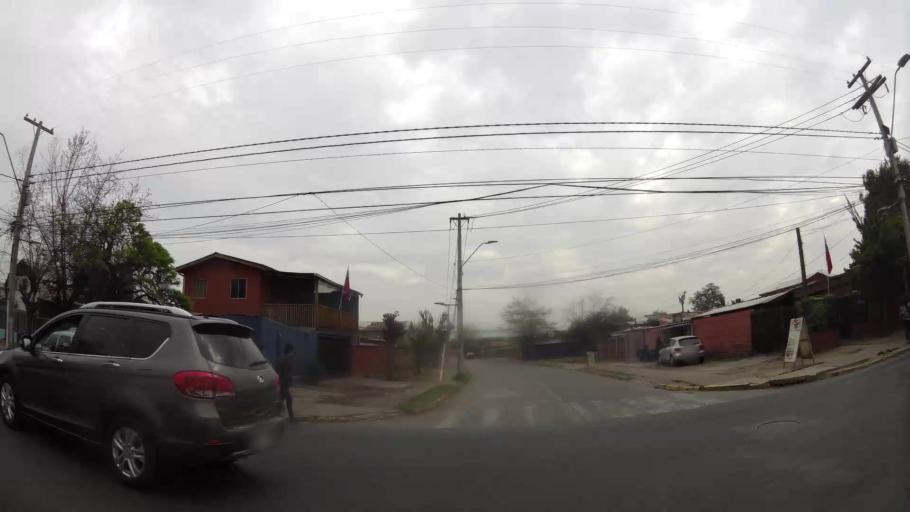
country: CL
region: Santiago Metropolitan
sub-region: Provincia de Santiago
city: Villa Presidente Frei, Nunoa, Santiago, Chile
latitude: -33.4772
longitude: -70.5882
